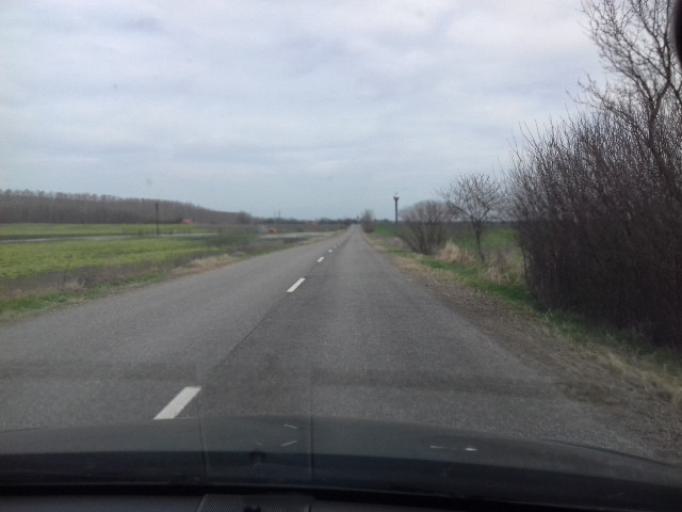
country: HU
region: Bacs-Kiskun
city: Tiszakecske
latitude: 46.8971
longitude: 20.1352
